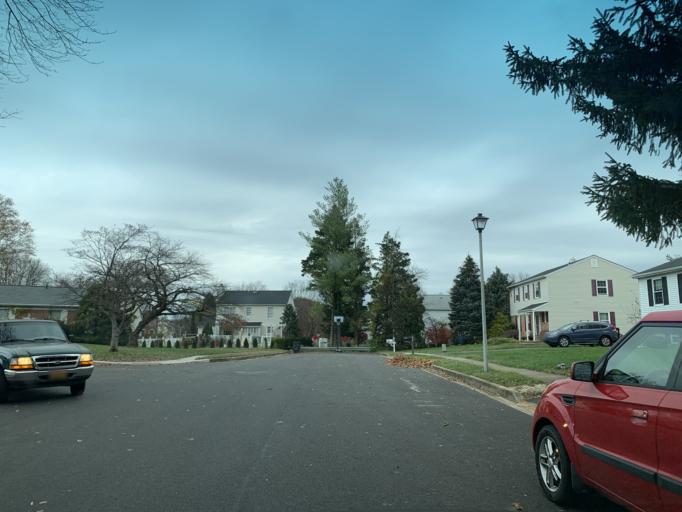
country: US
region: Maryland
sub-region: Harford County
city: Bel Air
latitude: 39.5449
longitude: -76.3457
